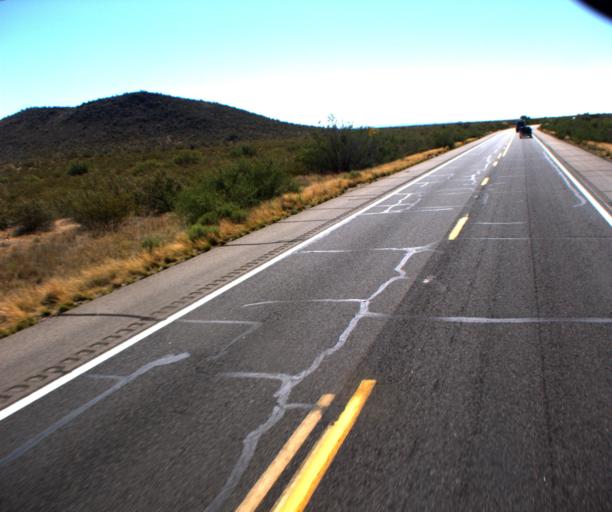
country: US
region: Arizona
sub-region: Yavapai County
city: Congress
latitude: 34.1747
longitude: -113.0250
